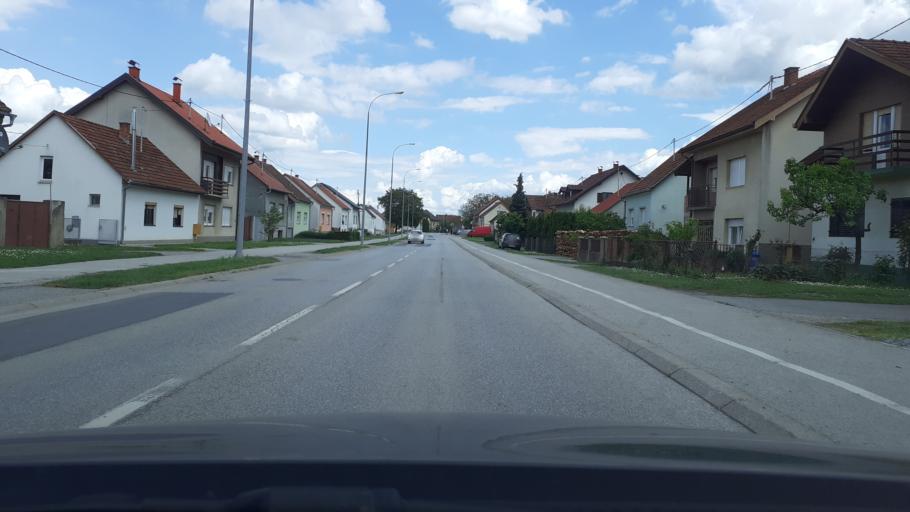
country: HR
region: Pozesko-Slavonska
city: Vidovci
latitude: 45.3340
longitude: 17.7031
